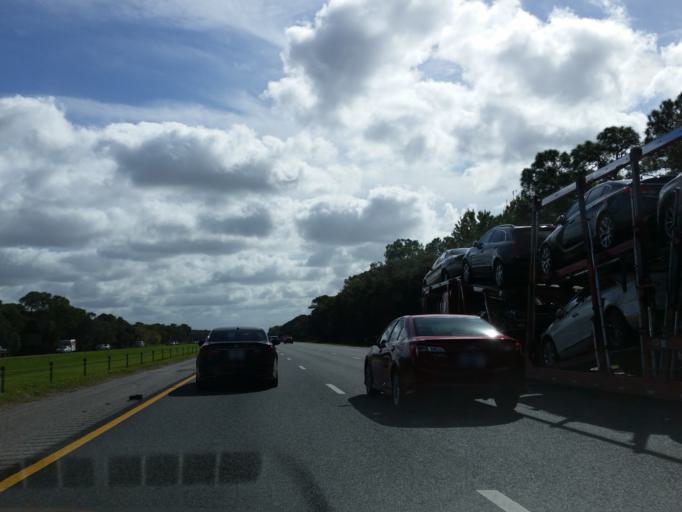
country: US
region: Florida
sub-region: Manatee County
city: Ellenton
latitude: 27.4814
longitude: -82.4677
